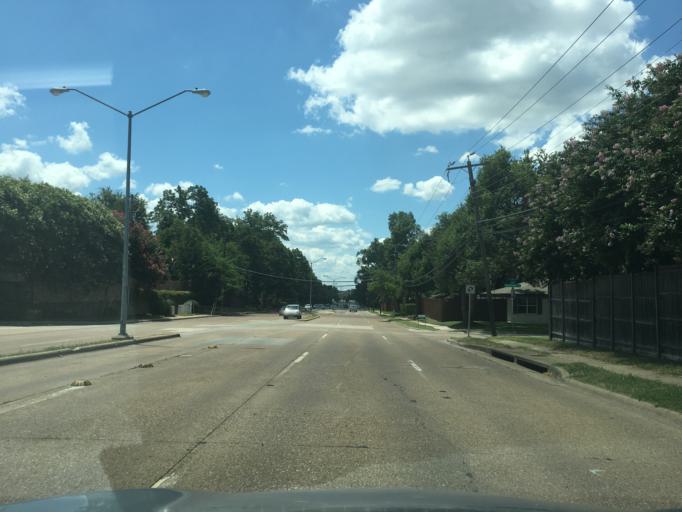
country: US
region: Texas
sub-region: Dallas County
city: Richardson
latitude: 32.8709
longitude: -96.7180
